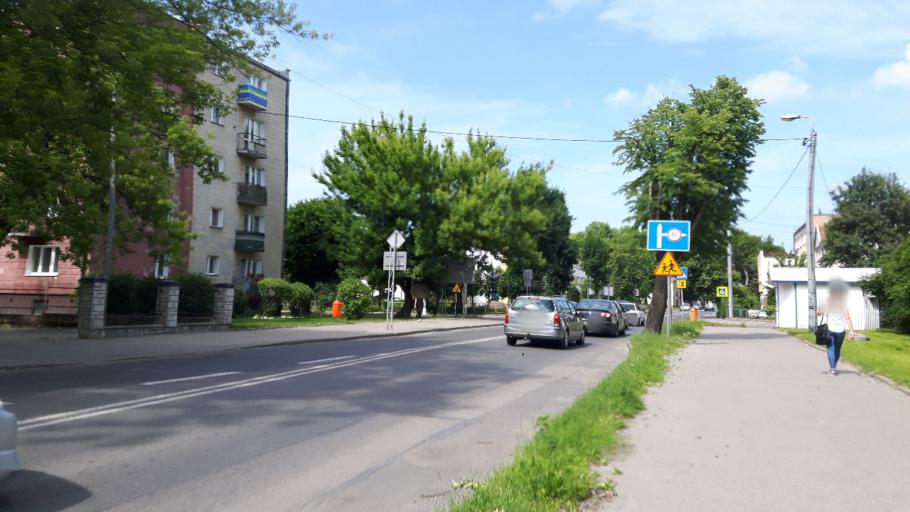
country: PL
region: Warmian-Masurian Voivodeship
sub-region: Powiat braniewski
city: Braniewo
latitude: 54.3849
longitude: 19.8290
